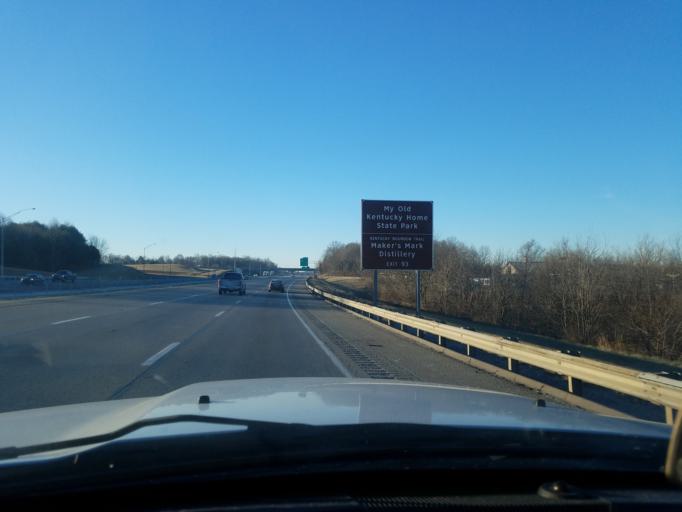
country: US
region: Kentucky
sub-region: Hardin County
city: Elizabethtown
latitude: 37.7079
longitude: -85.8307
